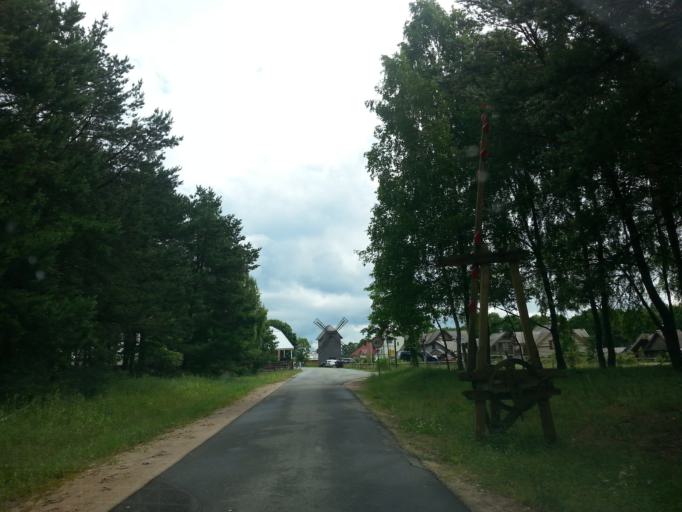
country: BY
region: Minsk
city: Narach
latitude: 54.8620
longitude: 26.7095
